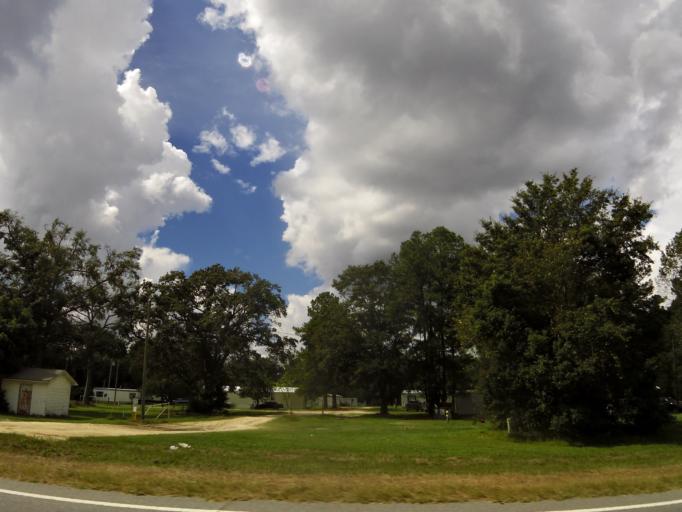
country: US
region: Georgia
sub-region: Brantley County
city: Nahunta
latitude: 31.1629
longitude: -81.9911
